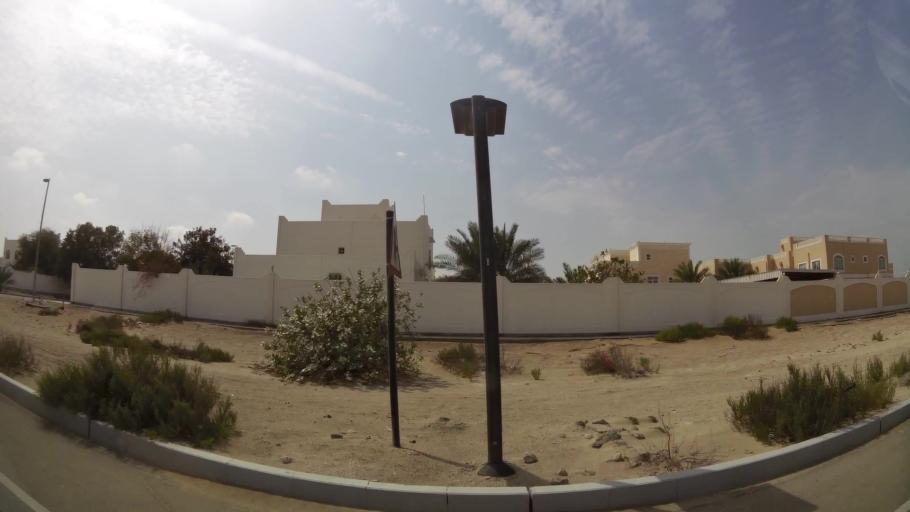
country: AE
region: Abu Dhabi
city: Abu Dhabi
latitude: 24.5597
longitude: 54.6388
